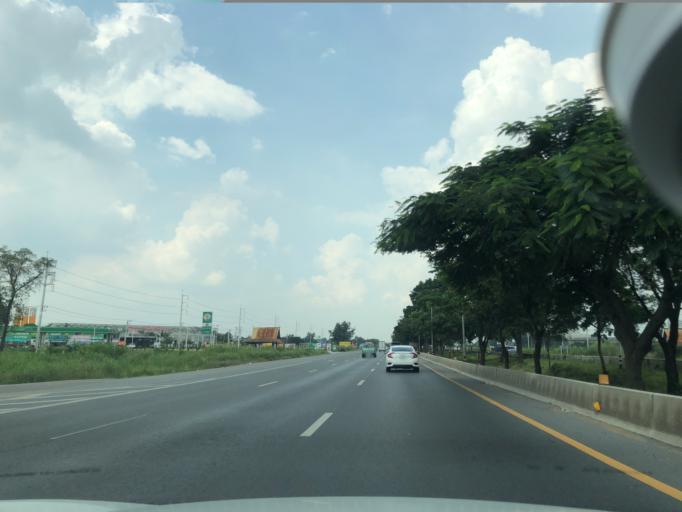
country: TH
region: Phra Nakhon Si Ayutthaya
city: Phra Nakhon Si Ayutthaya
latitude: 14.4045
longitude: 100.5845
